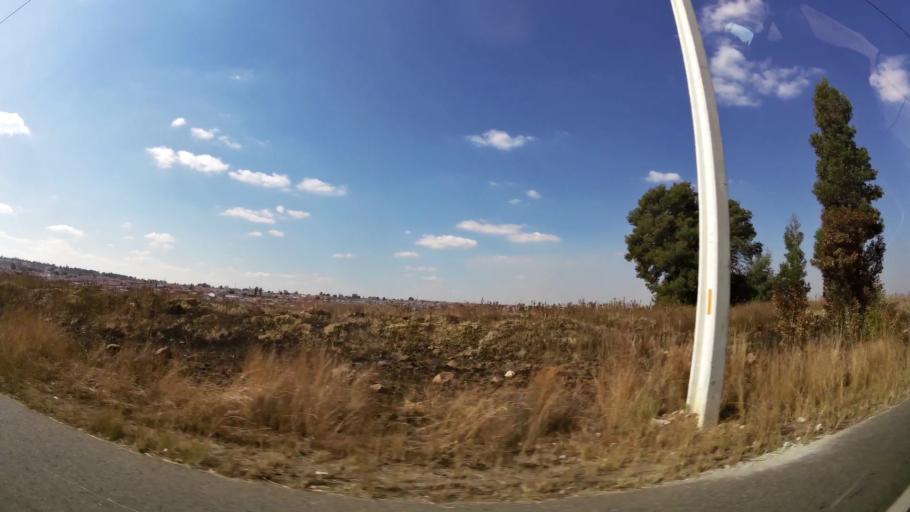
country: ZA
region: Gauteng
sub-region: West Rand District Municipality
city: Randfontein
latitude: -26.1595
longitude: 27.7620
